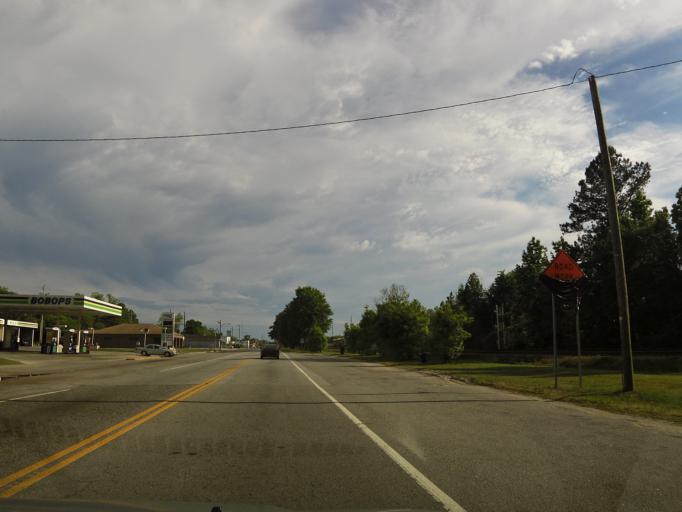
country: US
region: South Carolina
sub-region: Hampton County
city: Estill
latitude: 32.7599
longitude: -81.2412
